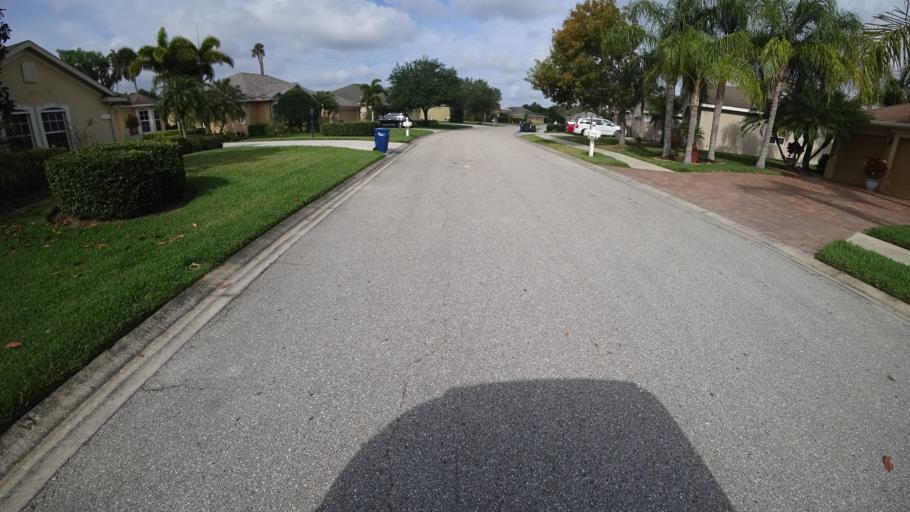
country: US
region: Florida
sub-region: Manatee County
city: Ellenton
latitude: 27.5703
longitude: -82.4705
